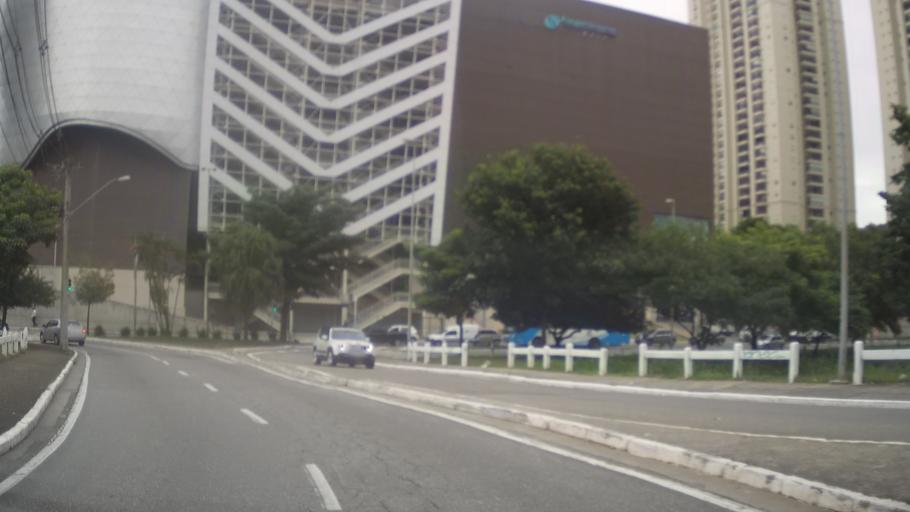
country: BR
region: Sao Paulo
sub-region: Guarulhos
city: Guarulhos
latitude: -23.4423
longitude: -46.5373
